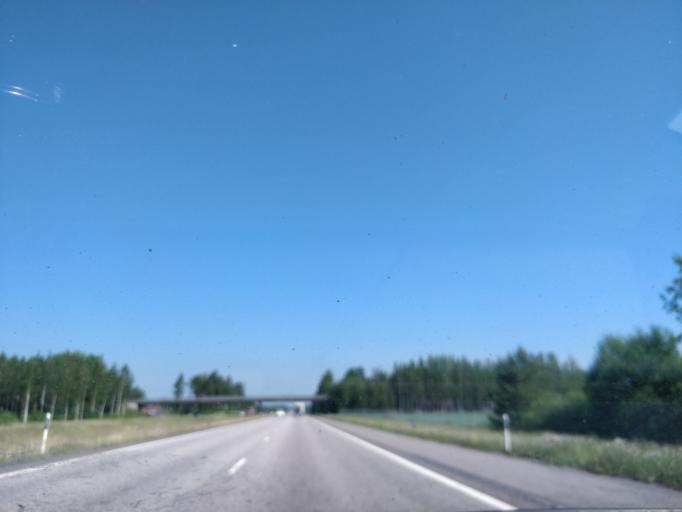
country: FI
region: Uusimaa
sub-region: Helsinki
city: Nurmijaervi
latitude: 60.5142
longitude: 24.8475
